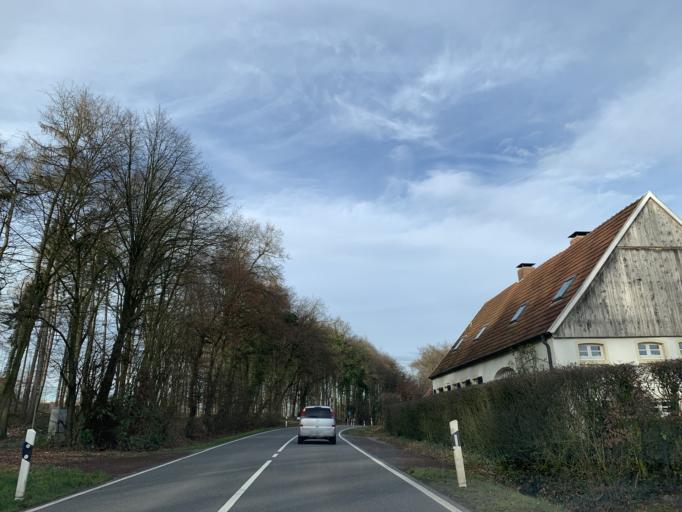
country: DE
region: North Rhine-Westphalia
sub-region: Regierungsbezirk Munster
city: Nottuln
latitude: 51.9404
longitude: 7.3343
